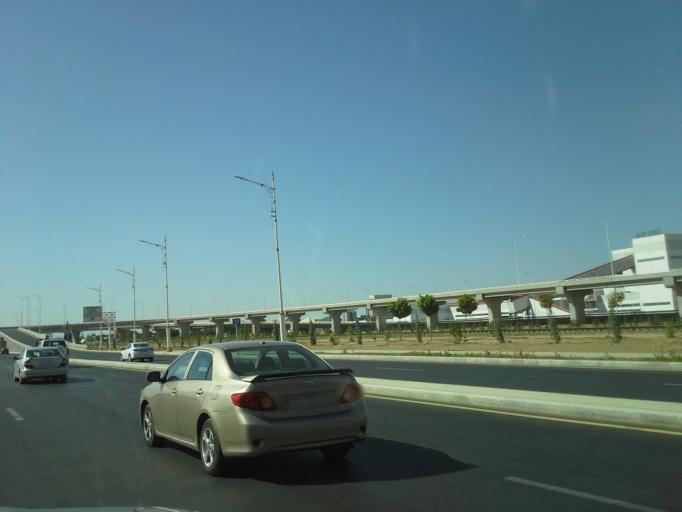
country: TM
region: Ahal
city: Ashgabat
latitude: 37.9274
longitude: 58.4273
